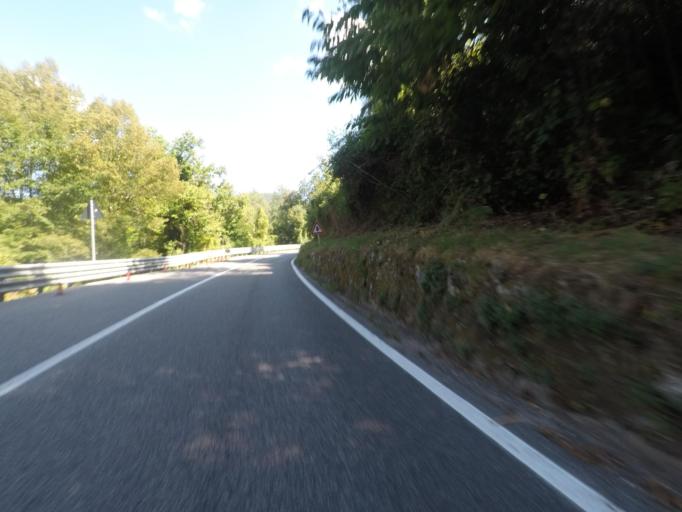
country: IT
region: Tuscany
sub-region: Provincia di Massa-Carrara
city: Fivizzano
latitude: 44.2435
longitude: 10.1552
